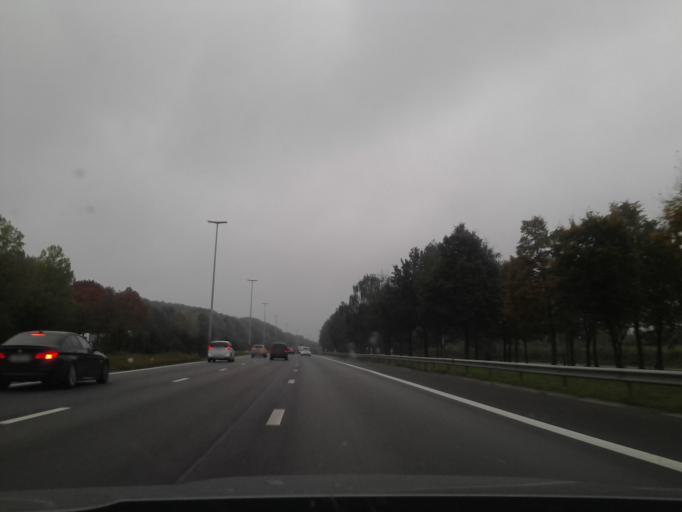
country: BE
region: Wallonia
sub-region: Province du Brabant Wallon
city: Braine-le-Chateau
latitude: 50.6978
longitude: 4.2834
